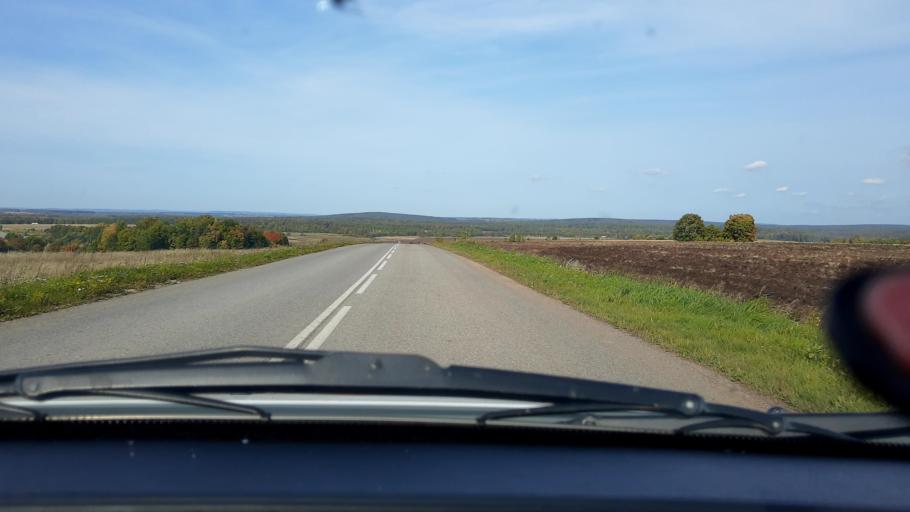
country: RU
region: Bashkortostan
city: Iglino
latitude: 54.7677
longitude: 56.5525
